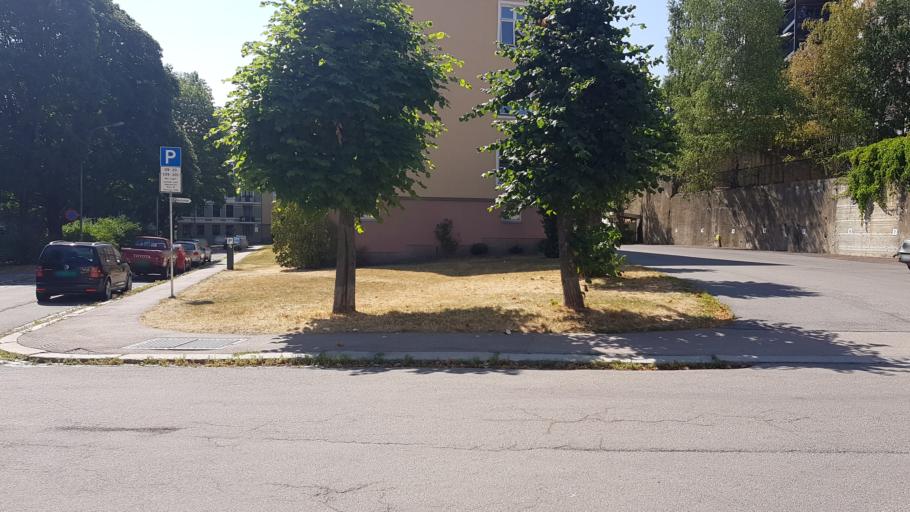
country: NO
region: Oslo
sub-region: Oslo
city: Oslo
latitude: 59.9300
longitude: 10.7475
